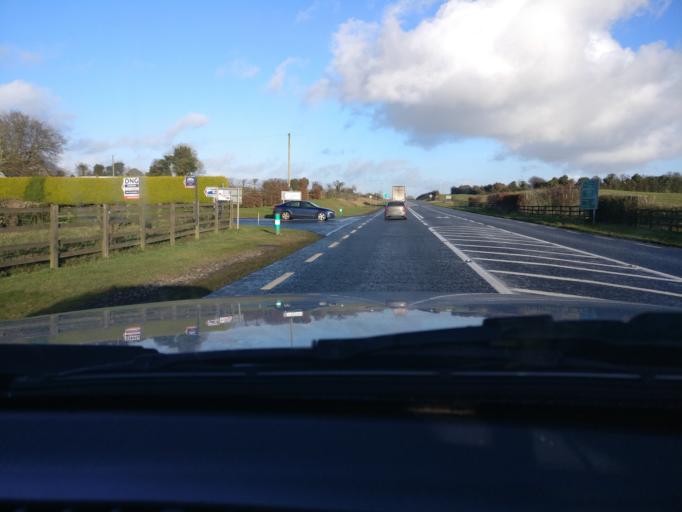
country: IE
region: Leinster
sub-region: An Iarmhi
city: Rathwire
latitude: 53.5958
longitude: -7.1136
